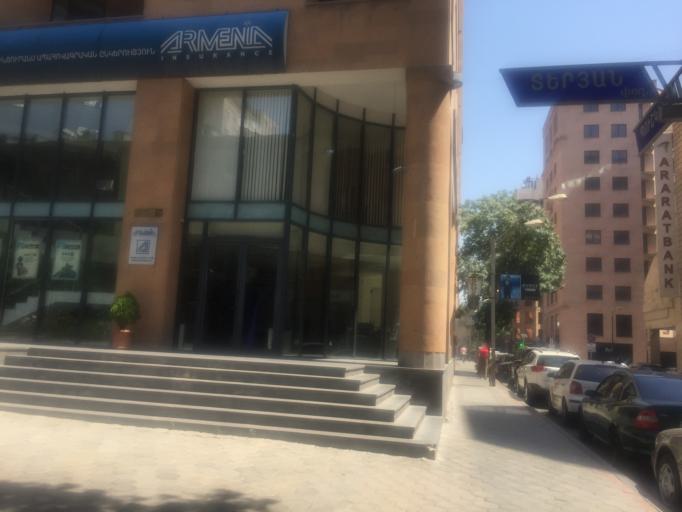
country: AM
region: Yerevan
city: Yerevan
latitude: 40.1820
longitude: 44.5137
